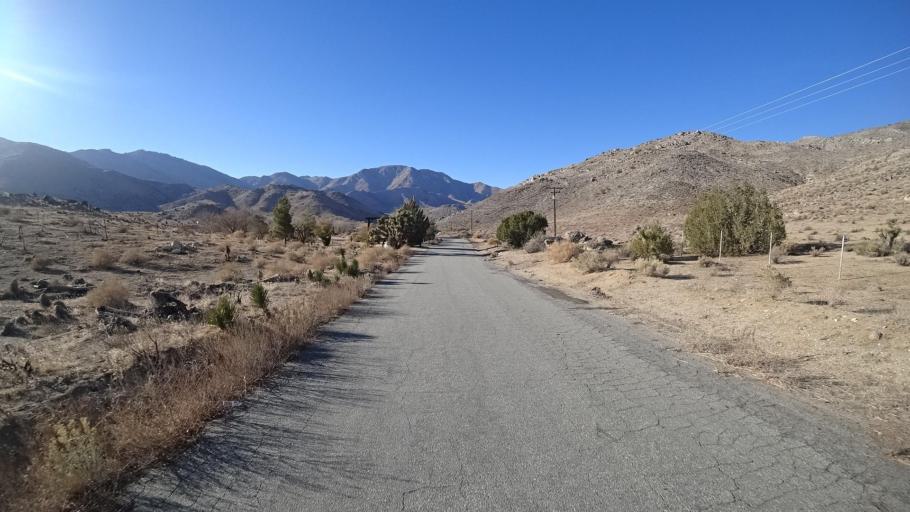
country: US
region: California
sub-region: Kern County
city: Weldon
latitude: 35.5639
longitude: -118.2413
